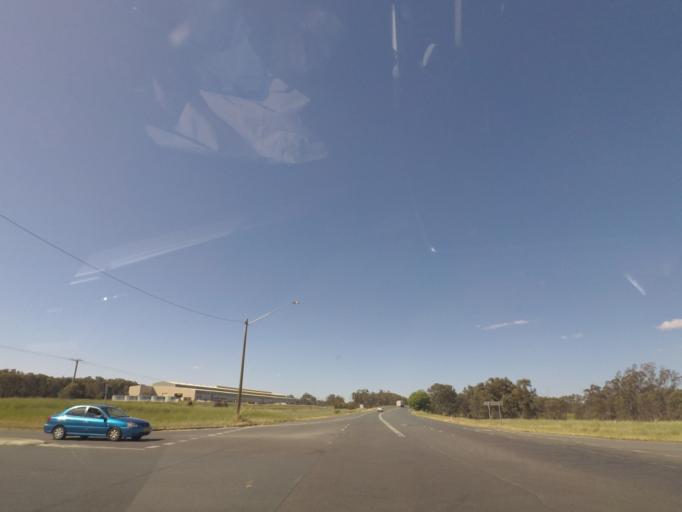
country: AU
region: New South Wales
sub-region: Albury Municipality
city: Lavington
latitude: -36.0060
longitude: 146.9851
